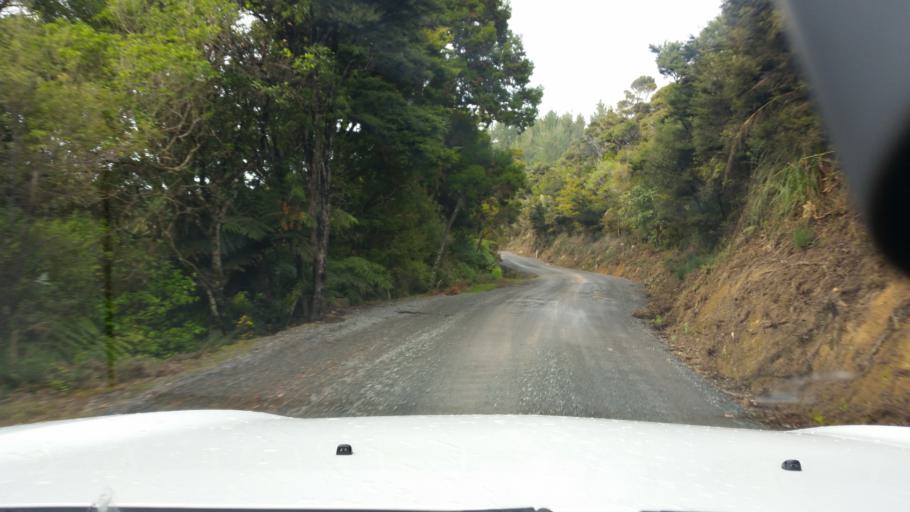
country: NZ
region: Northland
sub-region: Whangarei
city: Ngunguru
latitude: -35.7726
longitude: 174.5355
